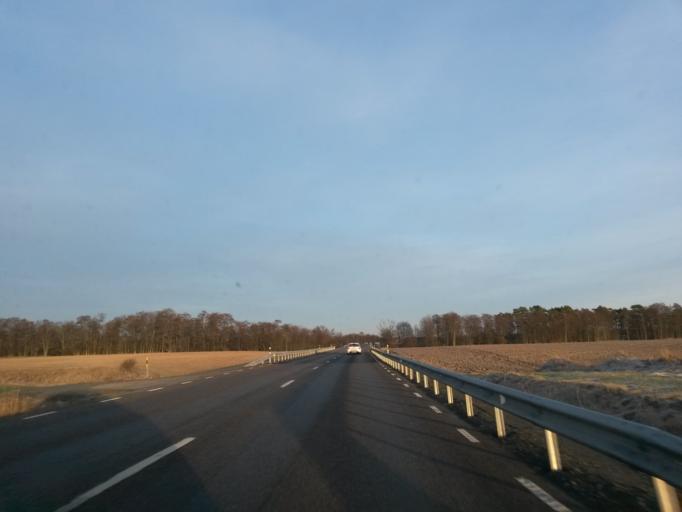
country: SE
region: Vaestra Goetaland
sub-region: Grastorps Kommun
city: Graestorp
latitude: 58.3467
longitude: 12.6385
